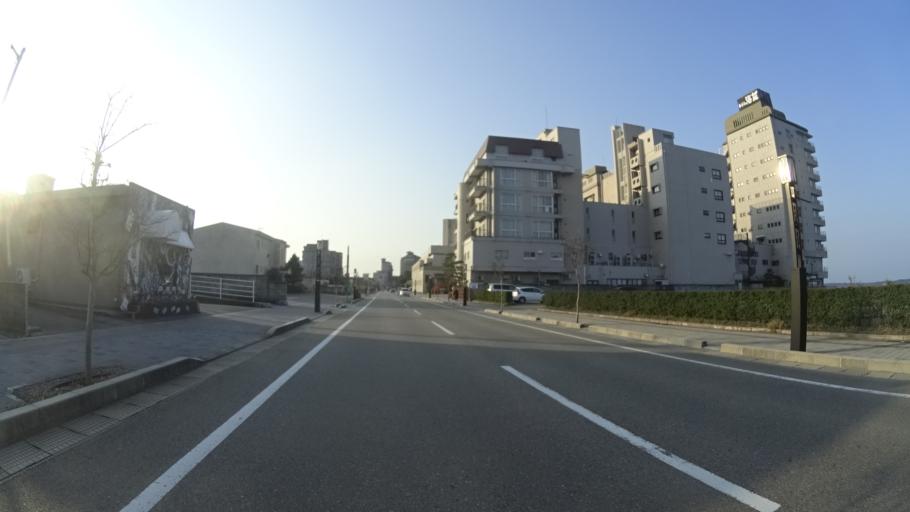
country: JP
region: Ishikawa
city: Nanao
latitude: 37.0874
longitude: 136.9224
